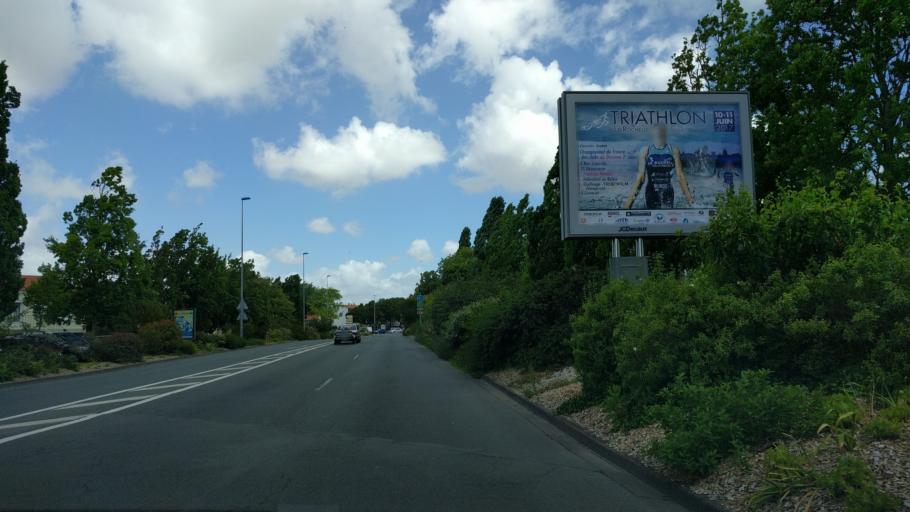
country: FR
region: Poitou-Charentes
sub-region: Departement de la Charente-Maritime
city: La Rochelle
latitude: 46.1648
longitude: -1.1366
